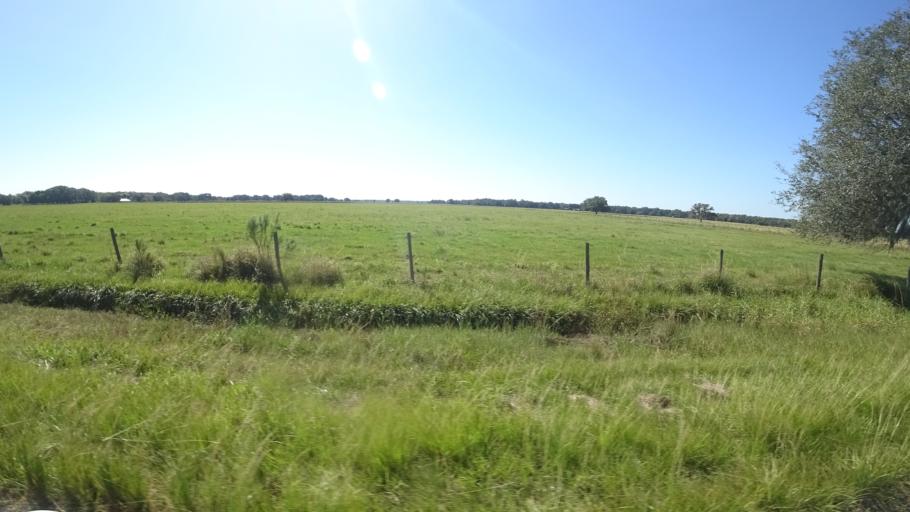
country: US
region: Florida
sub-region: Sarasota County
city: Warm Mineral Springs
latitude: 27.2739
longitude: -82.1868
